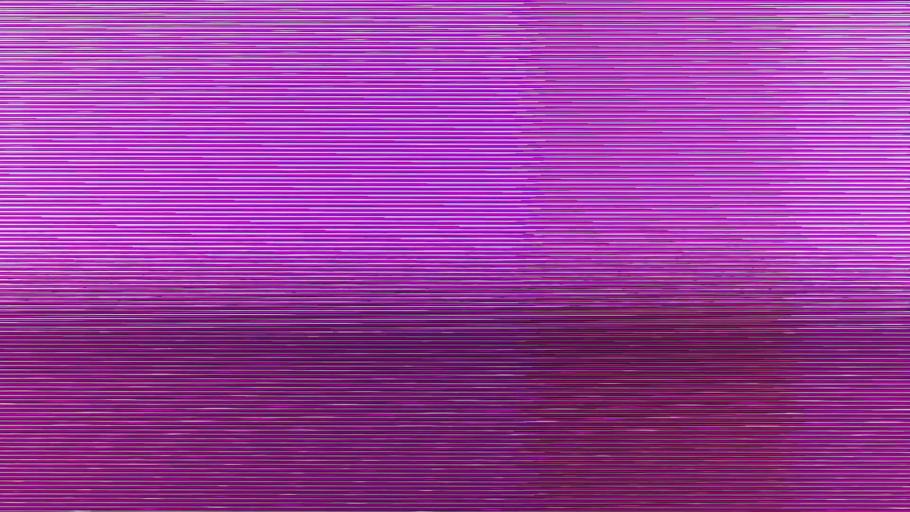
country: US
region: Wisconsin
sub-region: Racine County
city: Waterford
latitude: 42.7594
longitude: -88.2019
